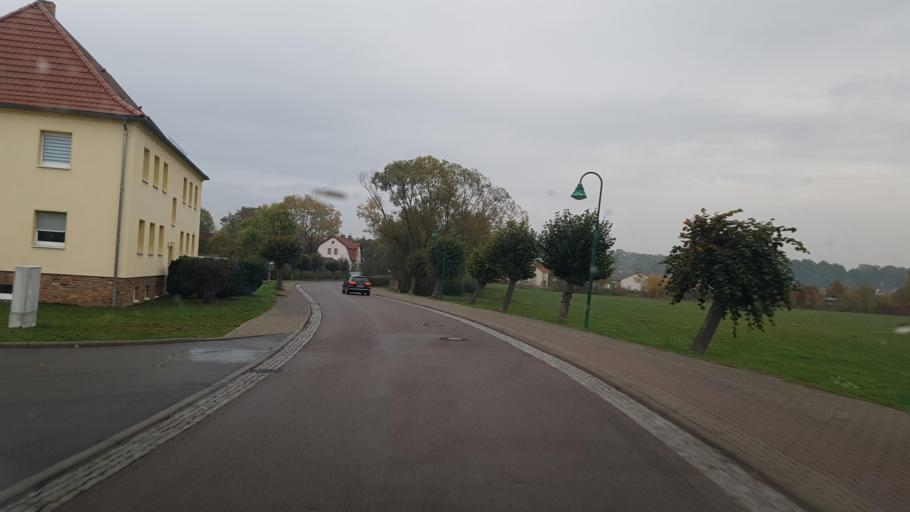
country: DE
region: Brandenburg
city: Schlieben
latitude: 51.7267
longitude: 13.3827
